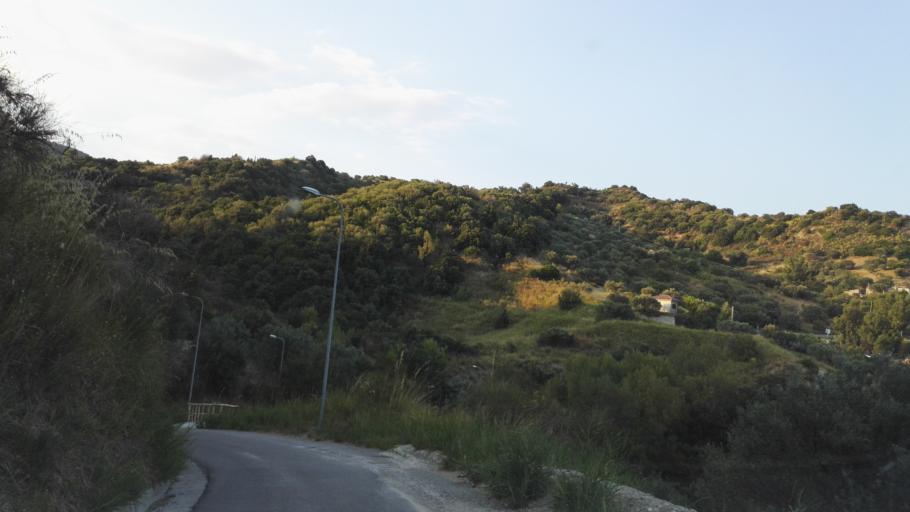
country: IT
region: Calabria
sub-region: Provincia di Reggio Calabria
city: Placanica
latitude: 38.4074
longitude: 16.4243
